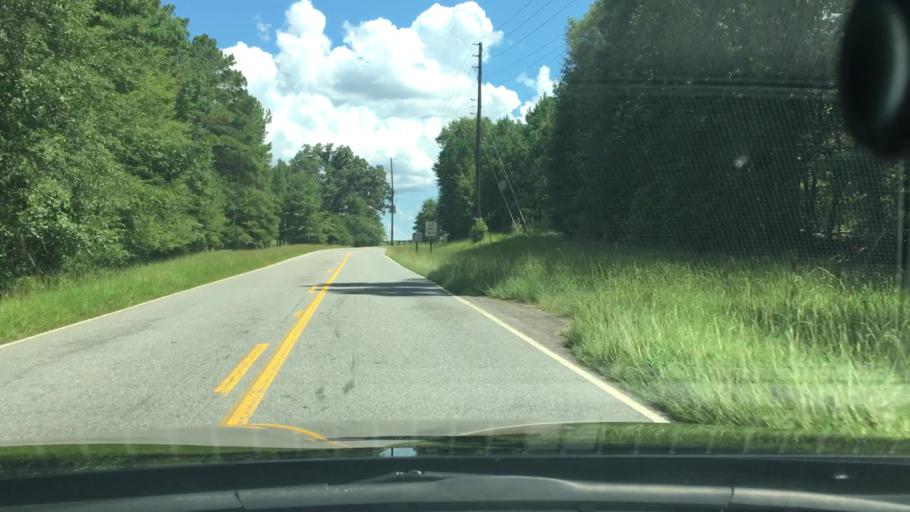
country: US
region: Georgia
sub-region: Putnam County
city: Jefferson
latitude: 33.3786
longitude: -83.2511
